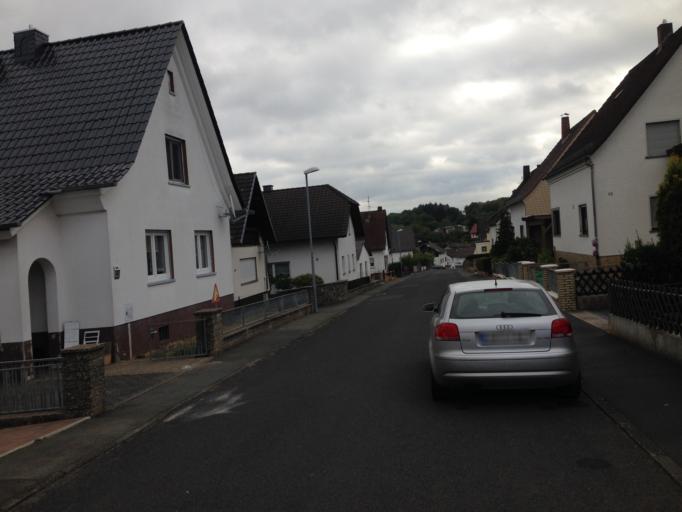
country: DE
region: Hesse
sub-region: Regierungsbezirk Giessen
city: Lohra
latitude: 50.6714
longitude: 8.5678
